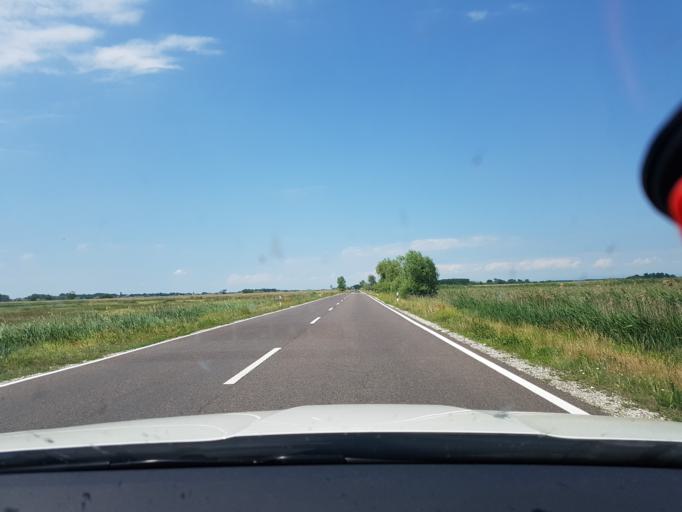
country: HU
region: Hajdu-Bihar
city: Egyek
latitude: 47.5547
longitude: 20.8736
